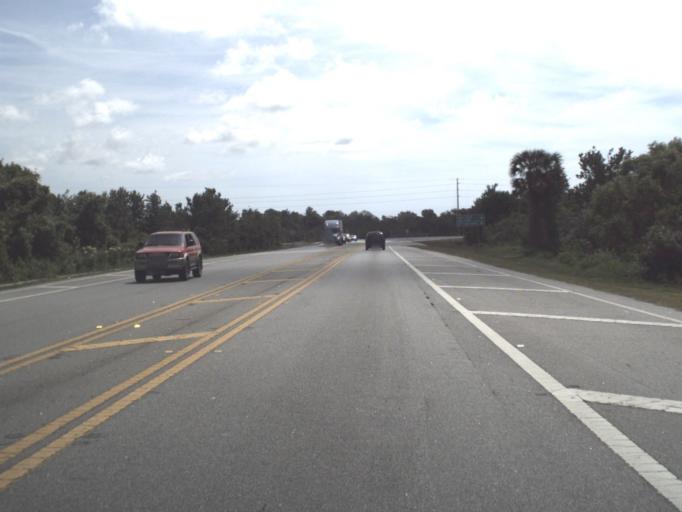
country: US
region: Florida
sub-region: Brevard County
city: Cocoa
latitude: 28.3970
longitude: -80.7585
